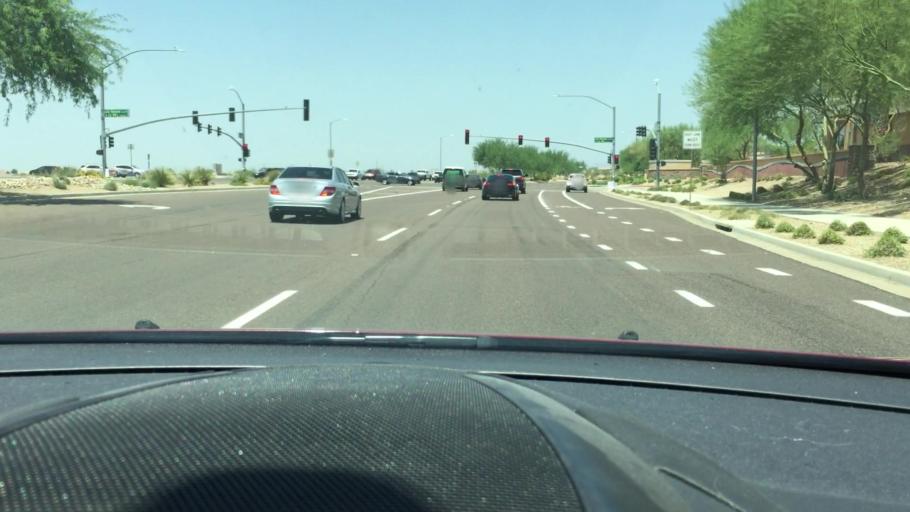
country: US
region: Arizona
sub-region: Maricopa County
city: Sun City West
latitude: 33.6771
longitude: -112.2773
